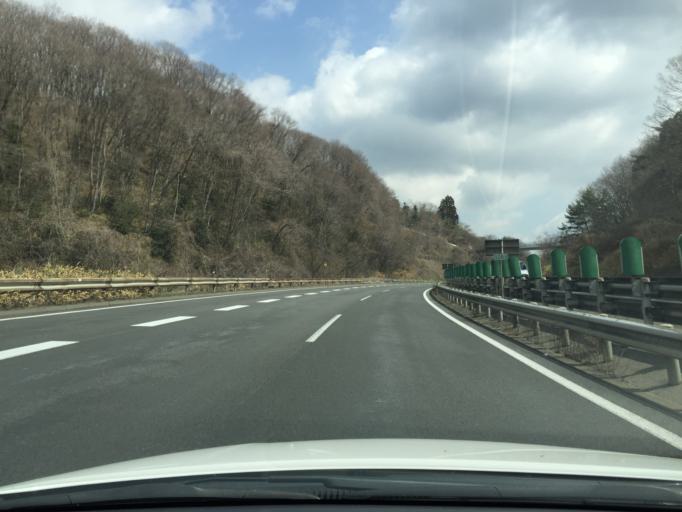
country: JP
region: Miyagi
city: Sendai
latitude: 38.2274
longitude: 140.8043
